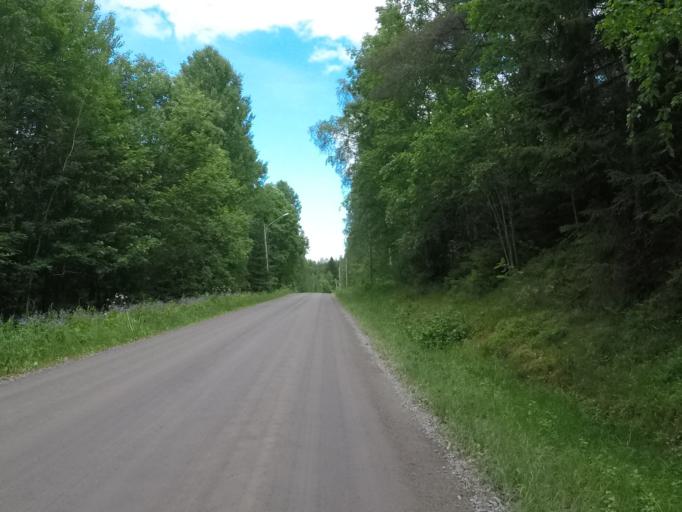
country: SE
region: Vaesterbotten
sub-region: Robertsfors Kommun
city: Robertsfors
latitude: 64.1462
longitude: 20.9056
